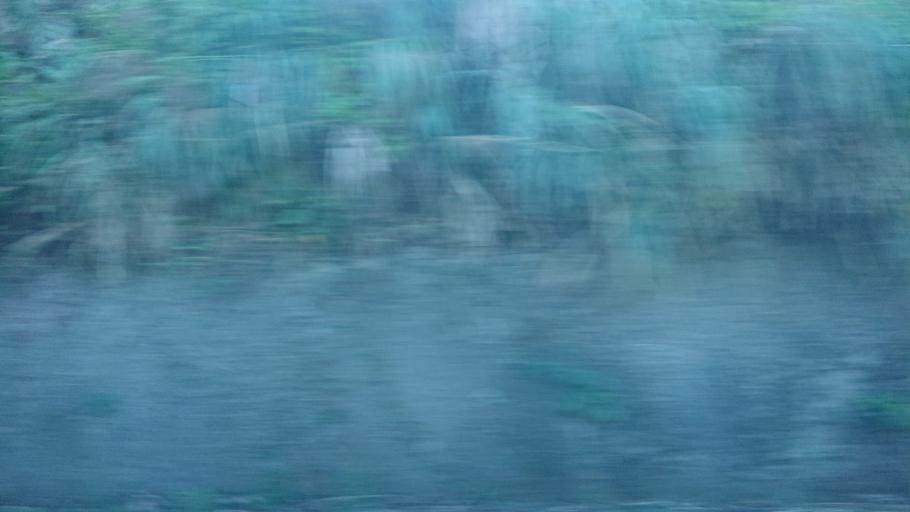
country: TW
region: Taiwan
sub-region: Chiayi
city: Jiayi Shi
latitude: 23.5183
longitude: 120.6245
